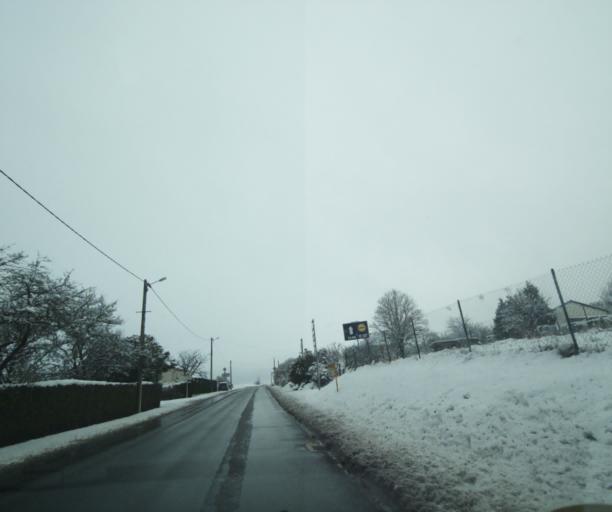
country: FR
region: Champagne-Ardenne
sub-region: Departement de la Haute-Marne
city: Montier-en-Der
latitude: 48.5322
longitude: 4.8164
